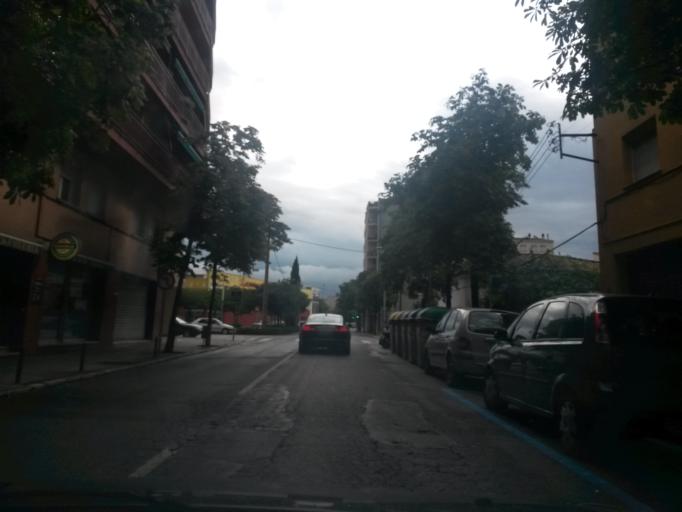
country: ES
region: Catalonia
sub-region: Provincia de Girona
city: Salt
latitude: 41.9688
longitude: 2.8110
